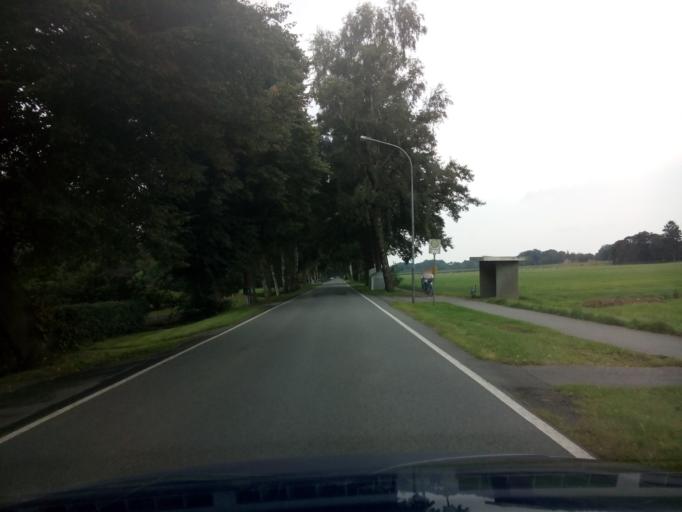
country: DE
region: Lower Saxony
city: Worpswede
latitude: 53.2403
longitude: 8.9800
